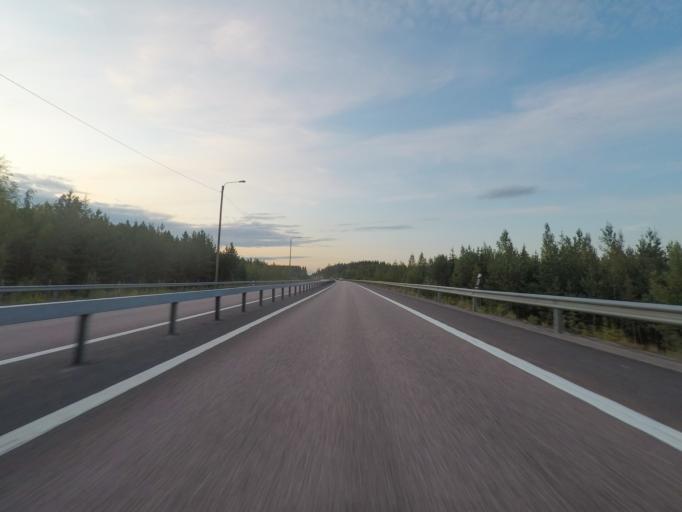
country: FI
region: Central Finland
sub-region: Jyvaeskylae
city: Saeynaetsalo
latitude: 62.1742
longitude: 25.9064
